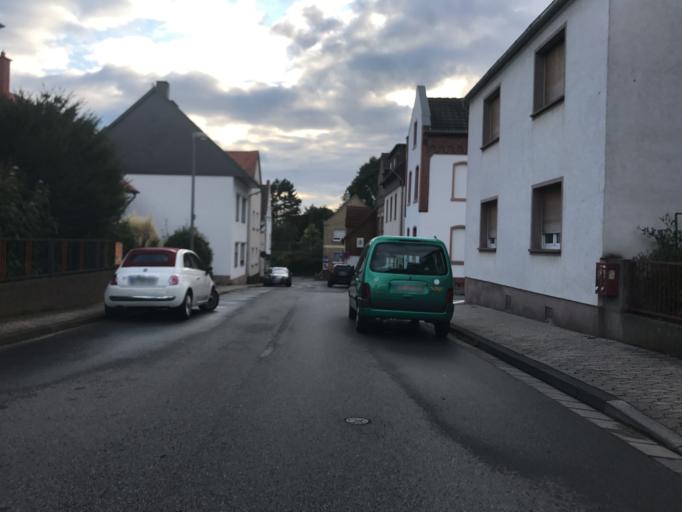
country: DE
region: Rheinland-Pfalz
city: Mainz
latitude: 49.9840
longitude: 8.2443
